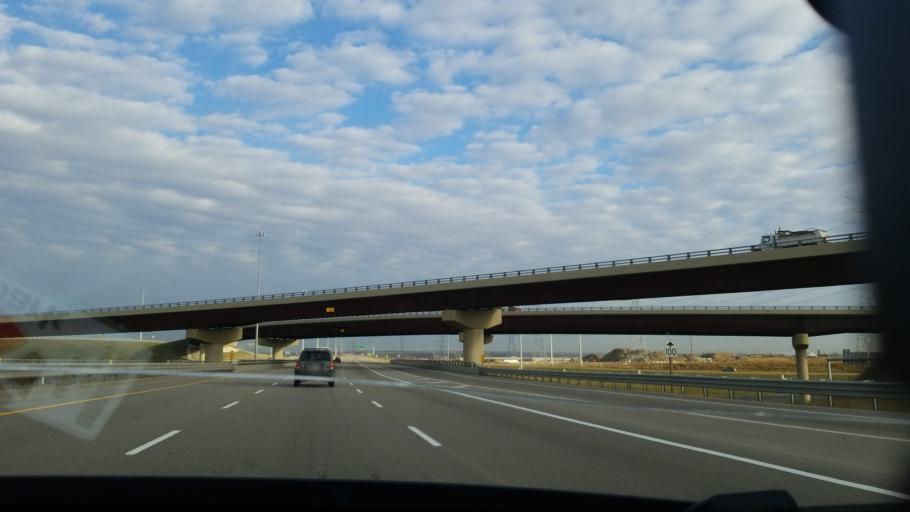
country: CA
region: Alberta
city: Sherwood Park
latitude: 53.5688
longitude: -113.3446
